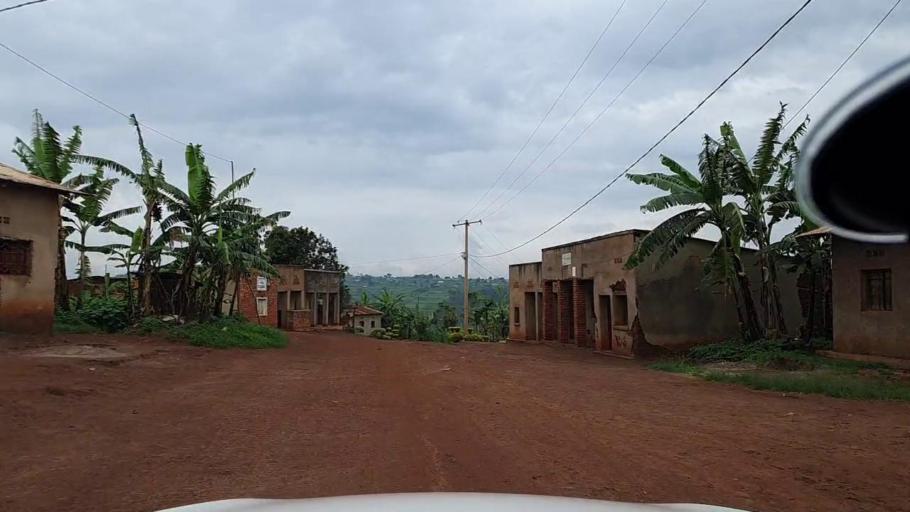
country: RW
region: Kigali
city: Kigali
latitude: -1.9115
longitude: 29.8983
